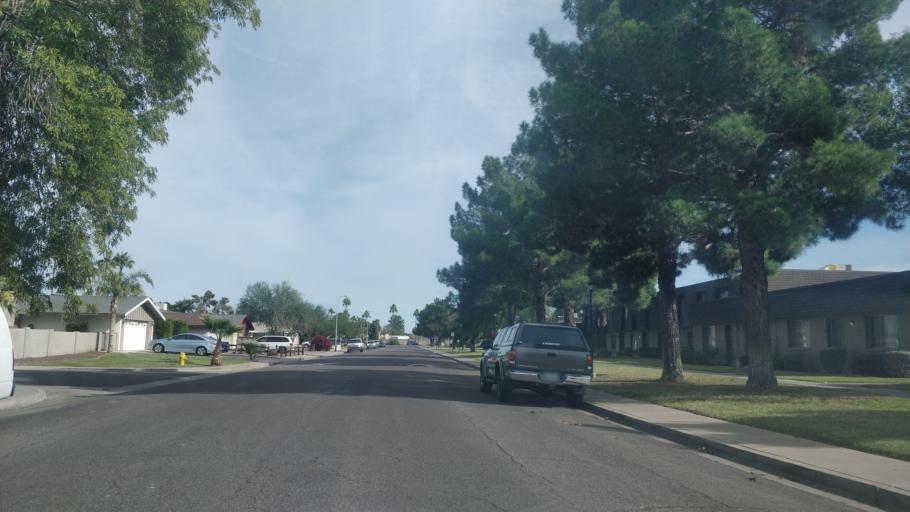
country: US
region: Arizona
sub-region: Maricopa County
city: Tempe
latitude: 33.3818
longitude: -111.9121
